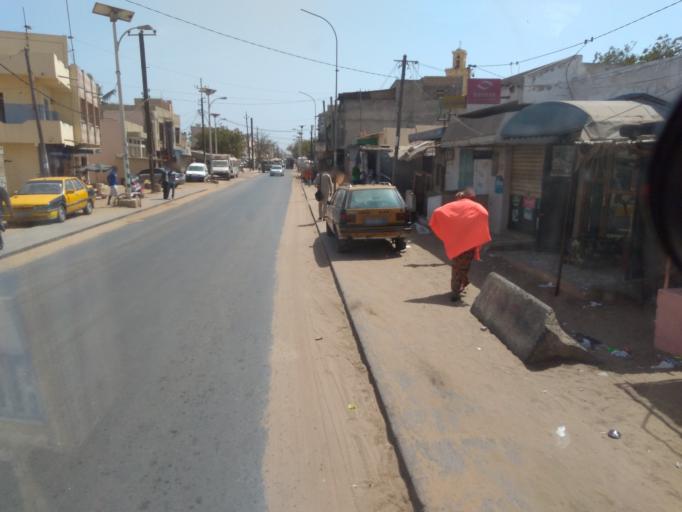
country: SN
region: Dakar
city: Pikine
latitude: 14.7688
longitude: -17.3656
